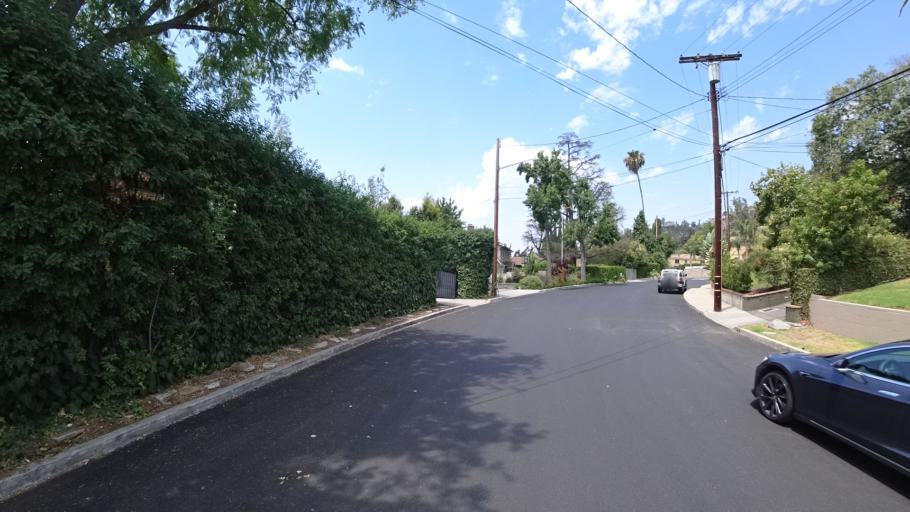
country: US
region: California
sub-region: Los Angeles County
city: Burbank
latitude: 34.1880
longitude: -118.2868
